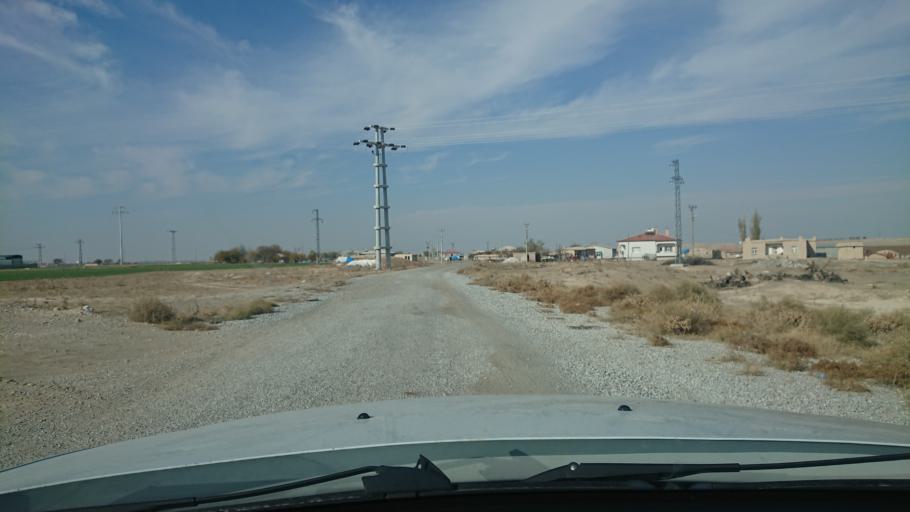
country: TR
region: Aksaray
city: Sultanhani
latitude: 38.2531
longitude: 33.4818
